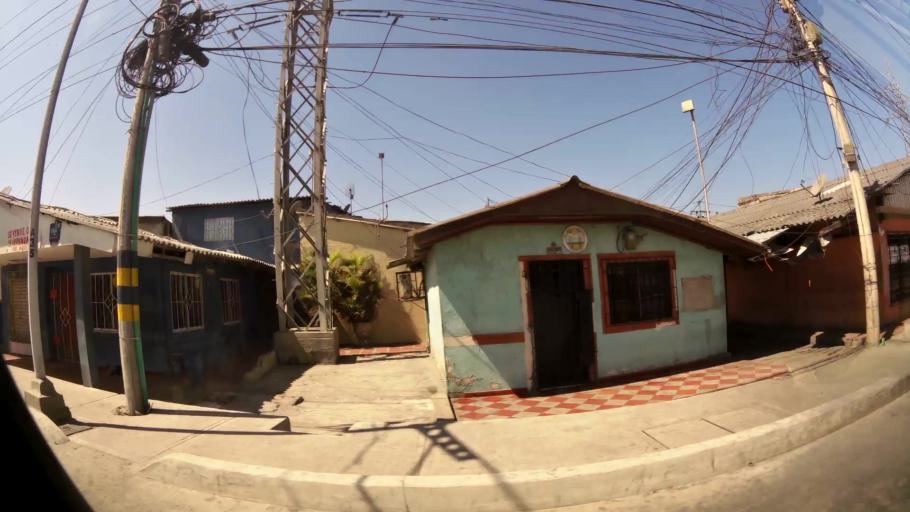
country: CO
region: Atlantico
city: Barranquilla
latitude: 10.9704
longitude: -74.7652
